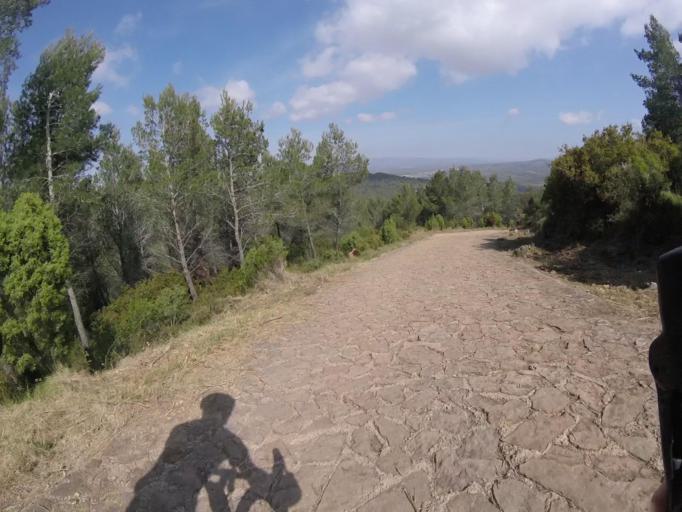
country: ES
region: Valencia
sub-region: Provincia de Castello
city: Benicassim
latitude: 40.0981
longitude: 0.0396
